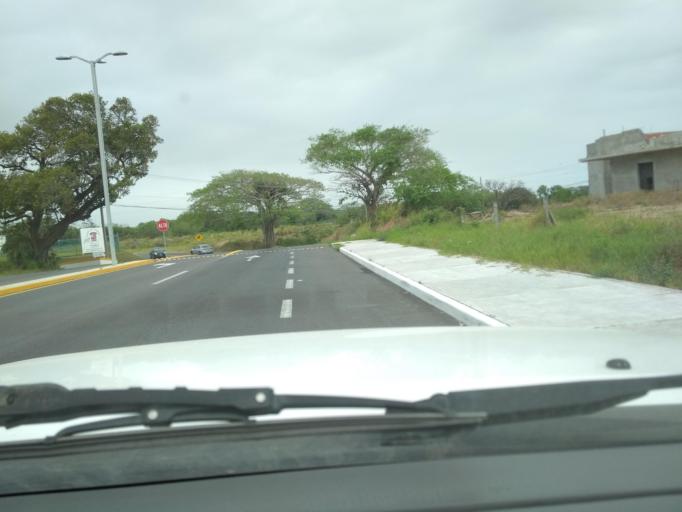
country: MX
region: Veracruz
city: Boca del Rio
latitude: 19.0892
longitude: -96.1199
